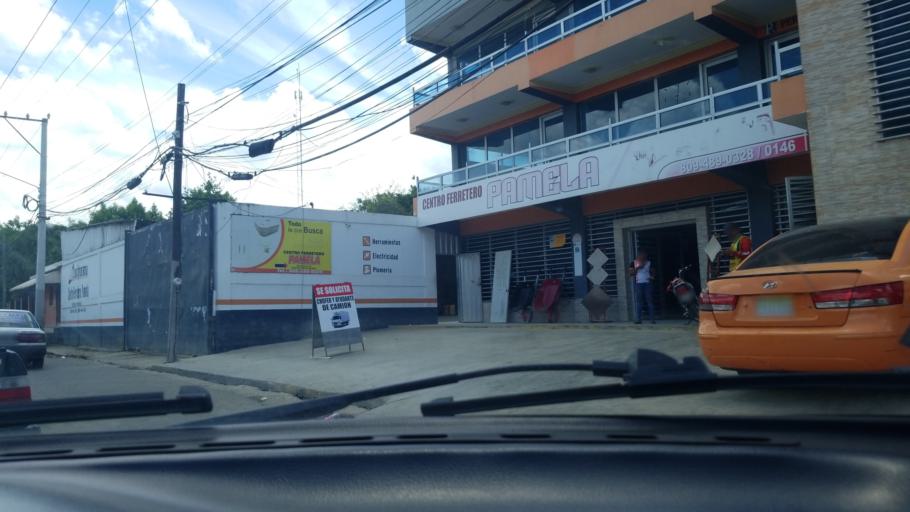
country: DO
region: Santiago
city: Santiago de los Caballeros
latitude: 19.4803
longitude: -70.6808
